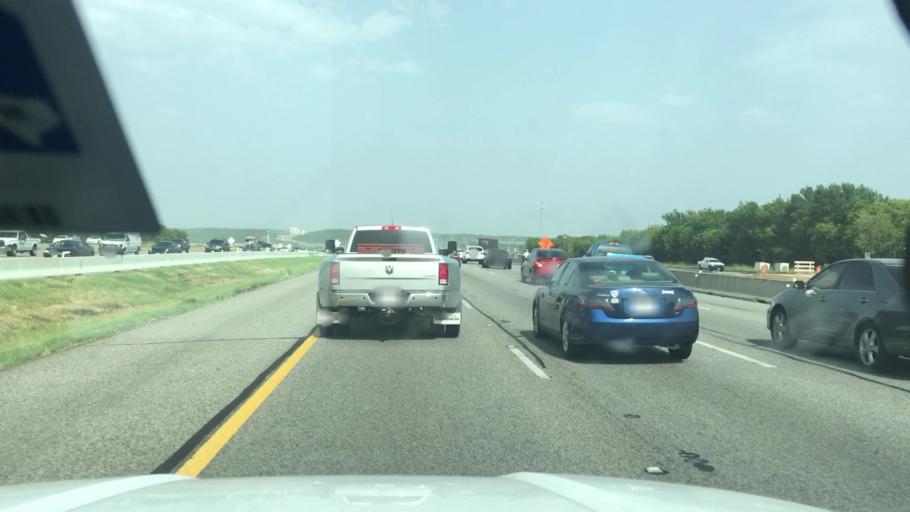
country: US
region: Texas
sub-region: Dallas County
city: Grand Prairie
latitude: 32.6736
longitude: -96.9947
